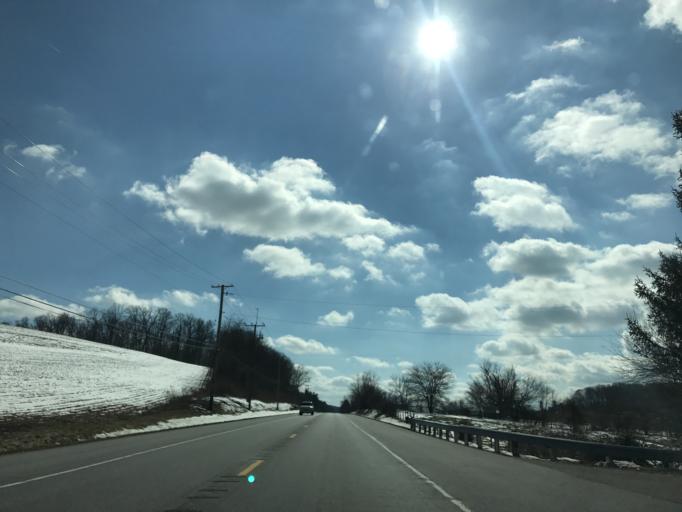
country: US
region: Maryland
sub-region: Carroll County
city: Manchester
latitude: 39.6493
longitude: -76.9115
